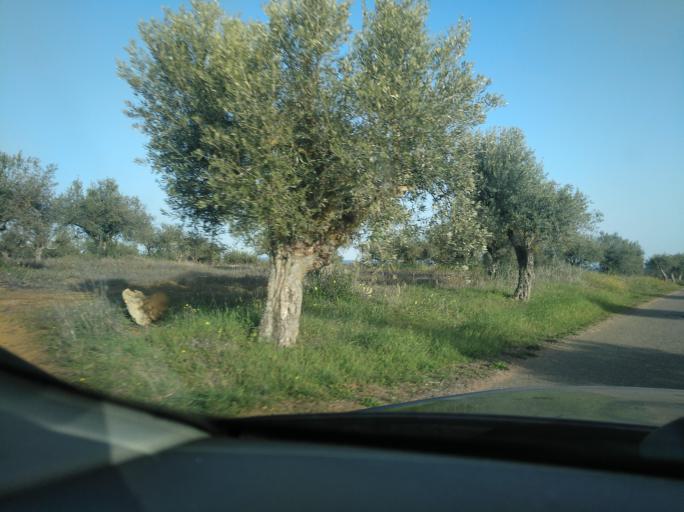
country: PT
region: Portalegre
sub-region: Campo Maior
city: Campo Maior
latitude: 39.0113
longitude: -7.0341
